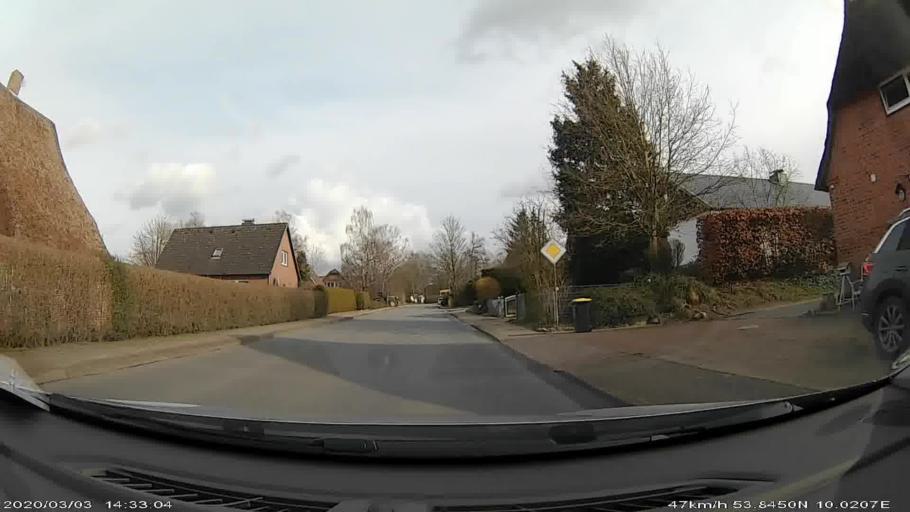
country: DE
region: Schleswig-Holstein
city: Kattendorf
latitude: 53.8451
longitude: 10.0208
